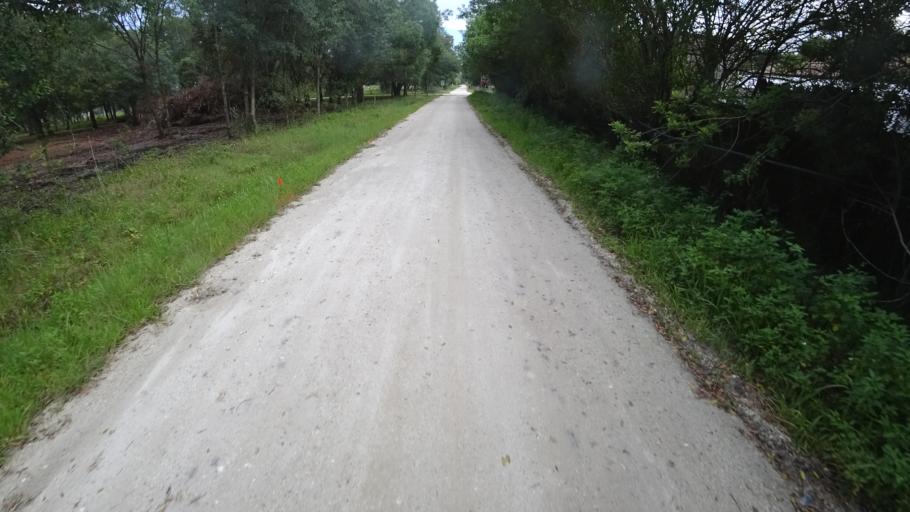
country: US
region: Florida
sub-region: Sarasota County
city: The Meadows
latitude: 27.4517
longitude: -82.2787
